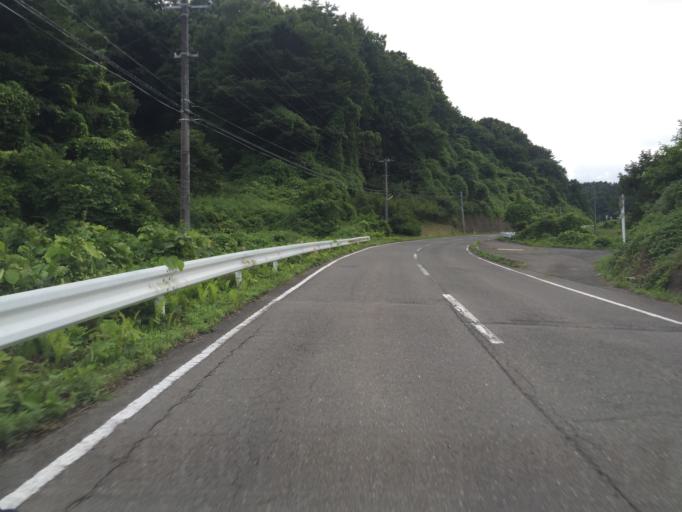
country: JP
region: Fukushima
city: Hobaramachi
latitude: 37.7094
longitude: 140.5851
